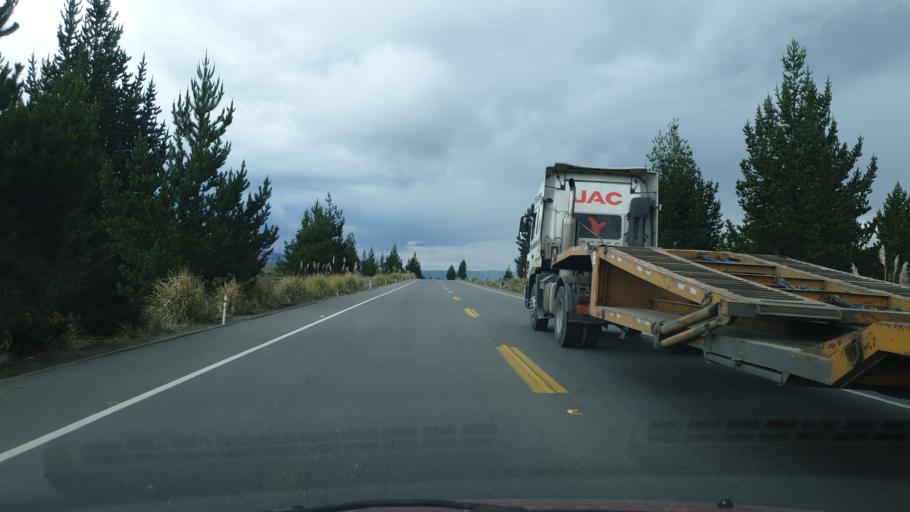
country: EC
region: Chimborazo
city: Alausi
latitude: -2.0315
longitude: -78.7355
